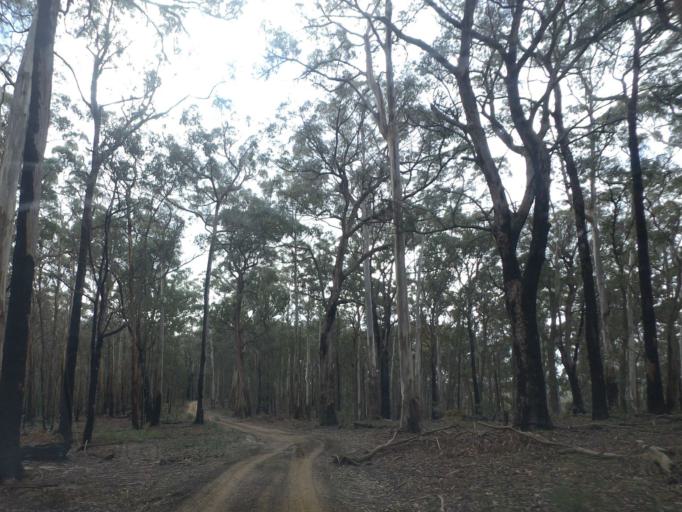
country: AU
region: Victoria
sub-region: Moorabool
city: Bacchus Marsh
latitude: -37.4515
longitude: 144.3257
